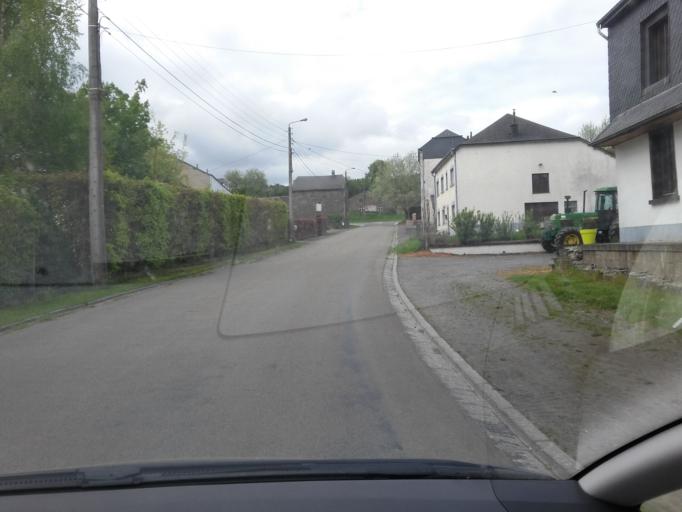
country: BE
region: Wallonia
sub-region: Province du Luxembourg
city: Bertrix
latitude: 49.8324
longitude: 5.3061
